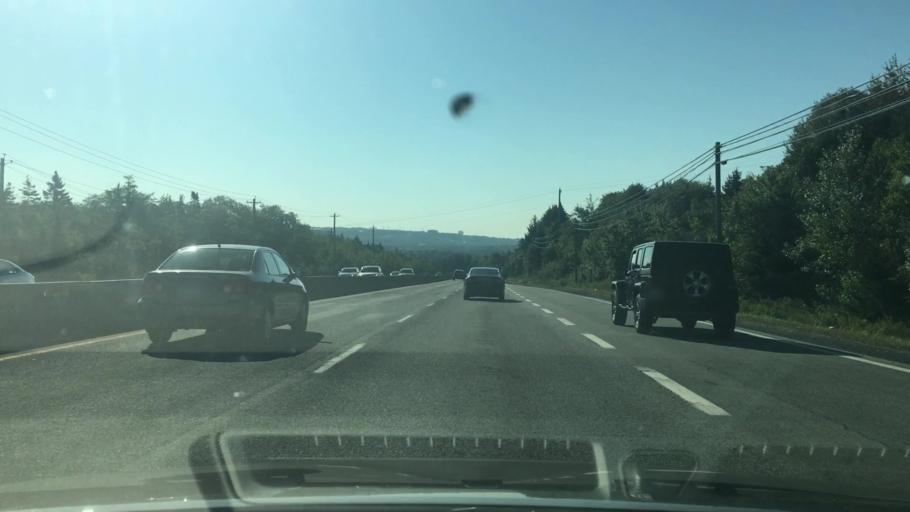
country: CA
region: Nova Scotia
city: Dartmouth
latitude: 44.7121
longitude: -63.6284
